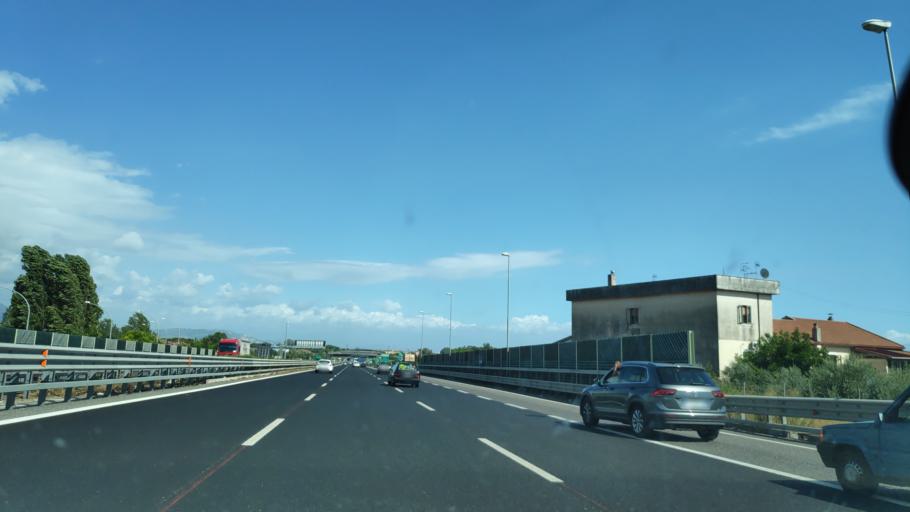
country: IT
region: Campania
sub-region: Provincia di Salerno
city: Pontecagnano
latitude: 40.6550
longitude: 14.8675
